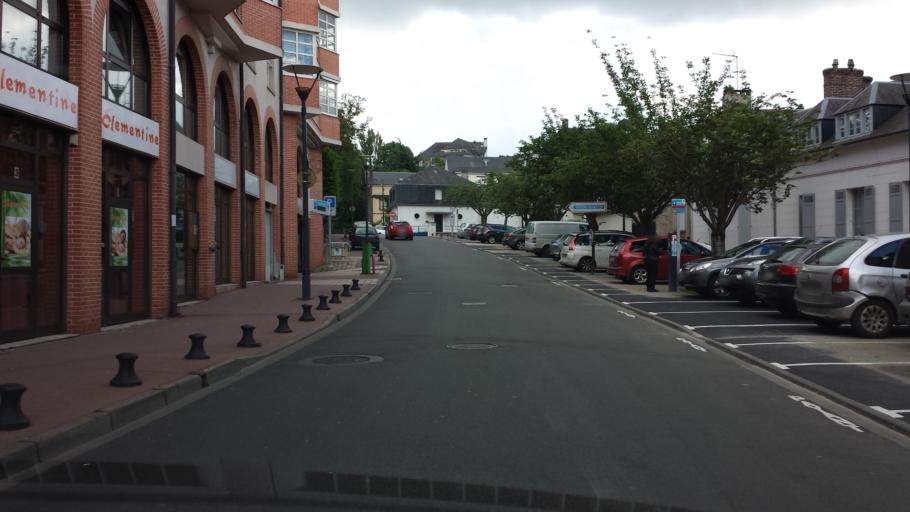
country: FR
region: Haute-Normandie
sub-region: Departement de l'Eure
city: Evreux
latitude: 49.0220
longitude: 1.1489
